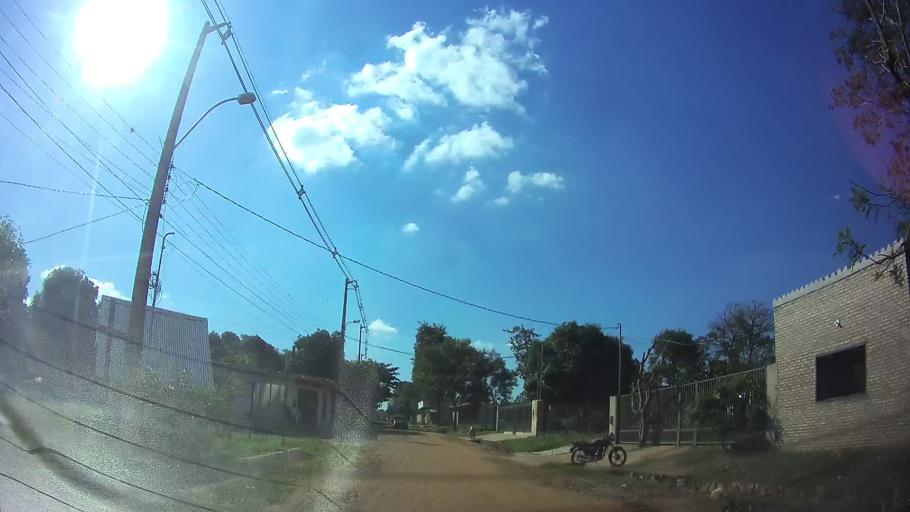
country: PY
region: Central
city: Limpio
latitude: -25.2457
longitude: -57.4743
